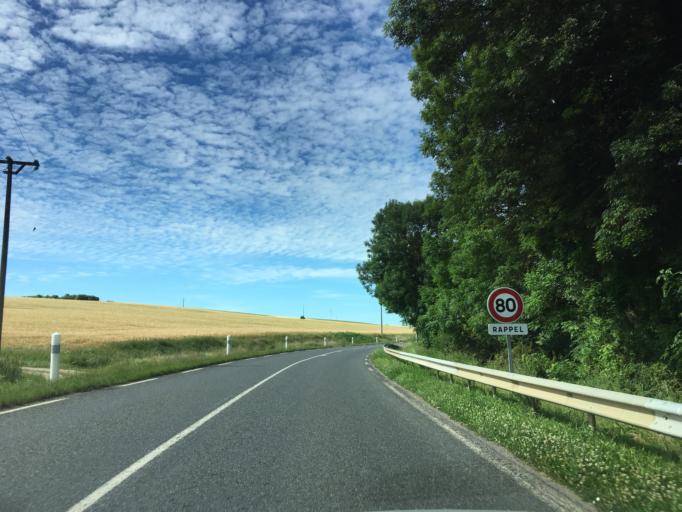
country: FR
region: Bourgogne
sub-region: Departement de l'Yonne
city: Auxerre
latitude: 47.7737
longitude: 3.5568
